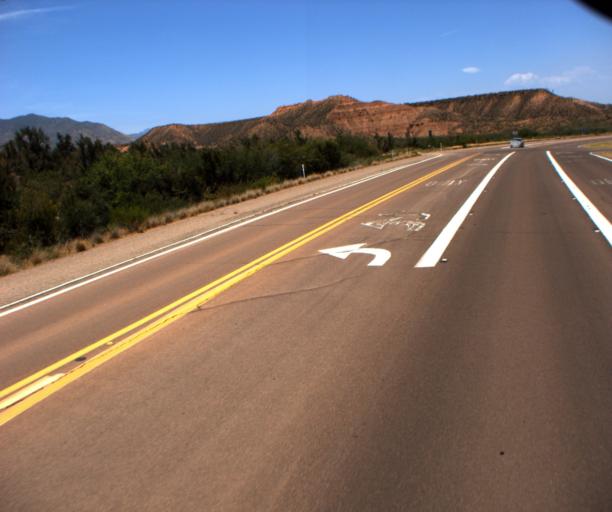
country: US
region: Arizona
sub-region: Gila County
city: Tonto Basin
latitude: 33.8759
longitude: -111.3157
